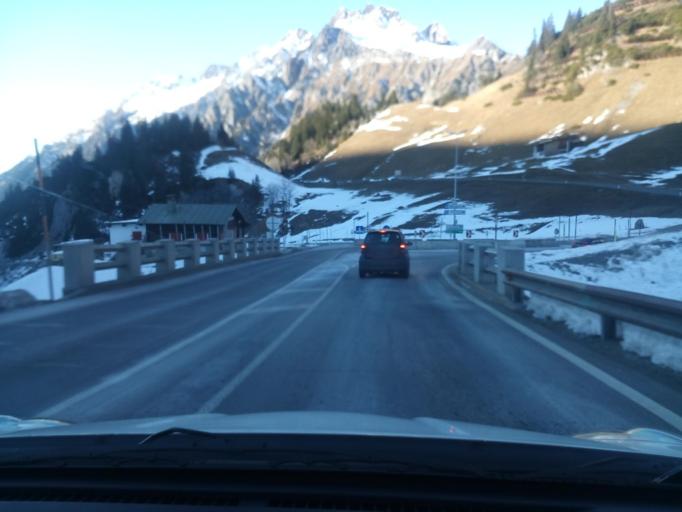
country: AT
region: Vorarlberg
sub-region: Politischer Bezirk Bludenz
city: Lech
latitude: 47.1376
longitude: 10.1761
